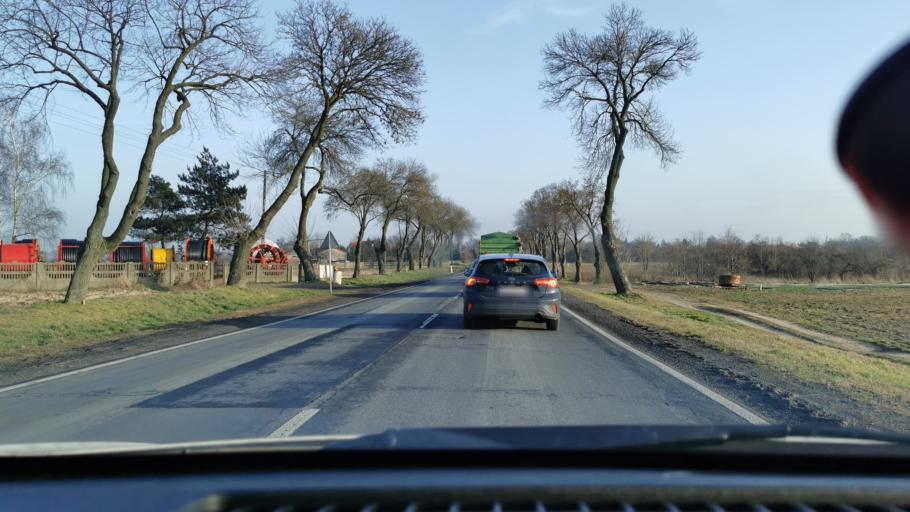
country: PL
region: Lodz Voivodeship
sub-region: Powiat sieradzki
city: Wroblew
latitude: 51.6150
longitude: 18.6046
